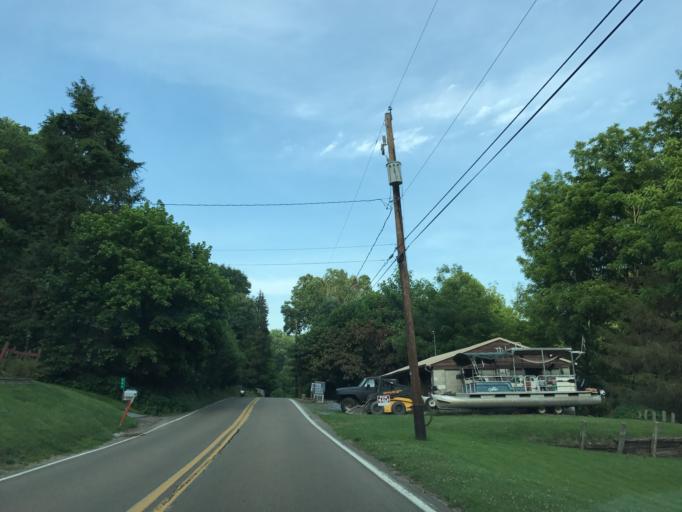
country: US
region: Pennsylvania
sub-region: Lancaster County
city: Conestoga
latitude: 39.8997
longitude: -76.3481
